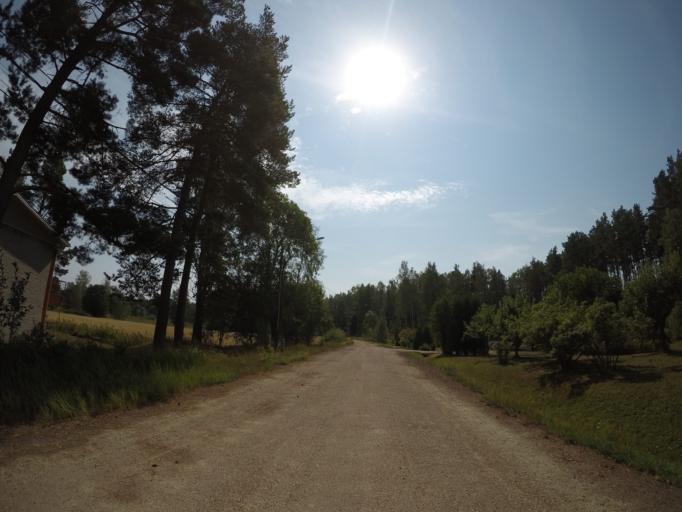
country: AX
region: Alands landsbygd
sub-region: Finstroem
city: Finstroem
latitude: 60.2332
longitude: 19.9807
